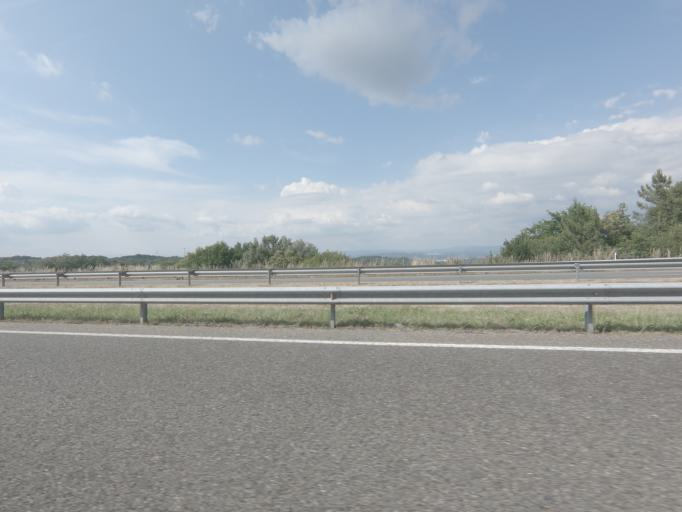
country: ES
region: Galicia
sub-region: Provincia de Ourense
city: Taboadela
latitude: 42.2361
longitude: -7.8536
